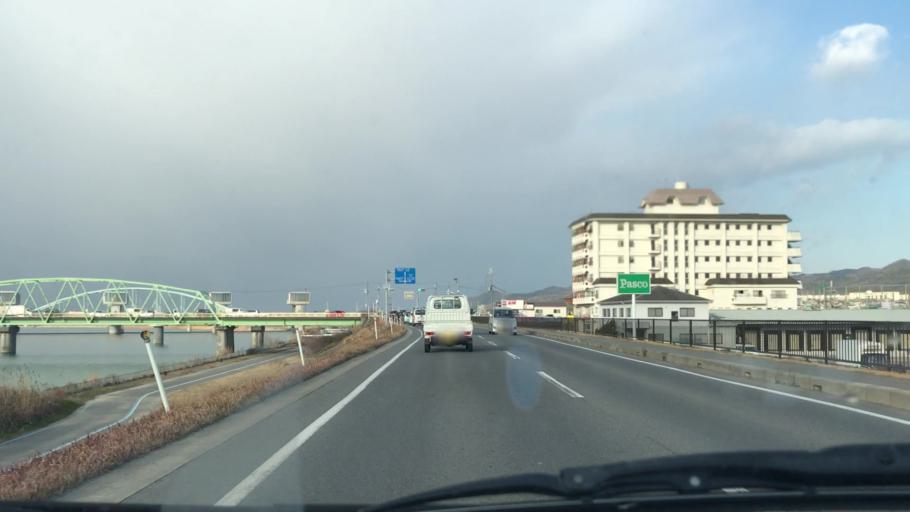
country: JP
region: Wakayama
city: Wakayama-shi
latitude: 34.2579
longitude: 135.2023
